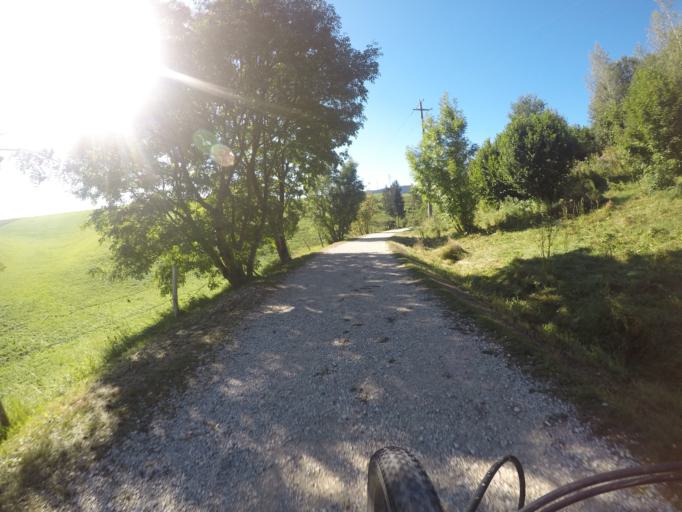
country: IT
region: Veneto
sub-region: Provincia di Vicenza
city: Canove di Roana
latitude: 45.8601
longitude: 11.4764
